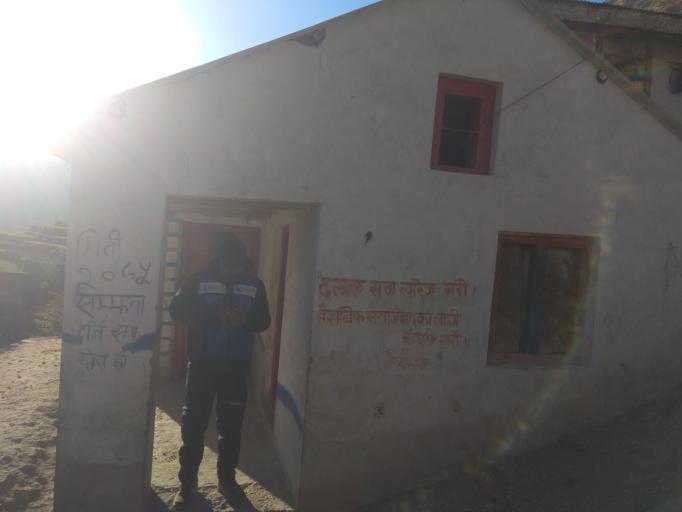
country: NP
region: Mid Western
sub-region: Bheri Zone
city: Dailekh
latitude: 29.2600
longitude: 81.6809
